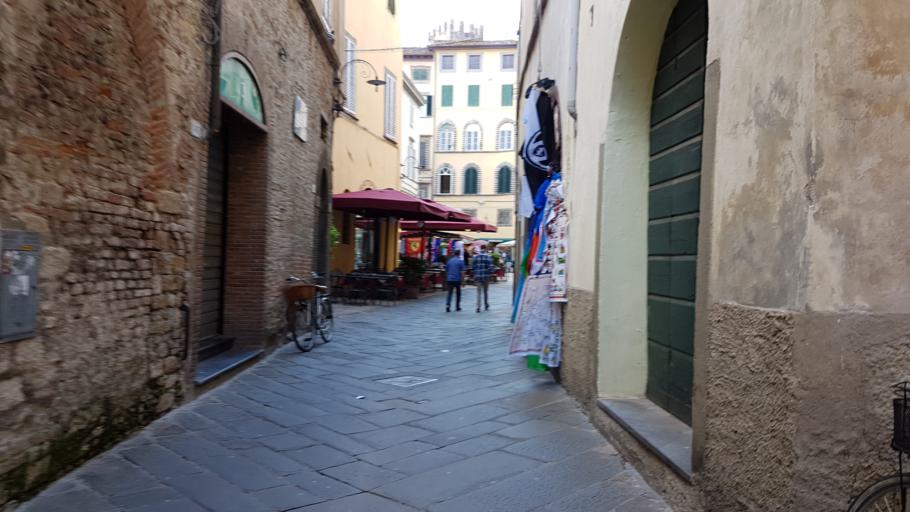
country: IT
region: Tuscany
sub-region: Provincia di Lucca
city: Lucca
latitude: 43.8452
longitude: 10.5059
